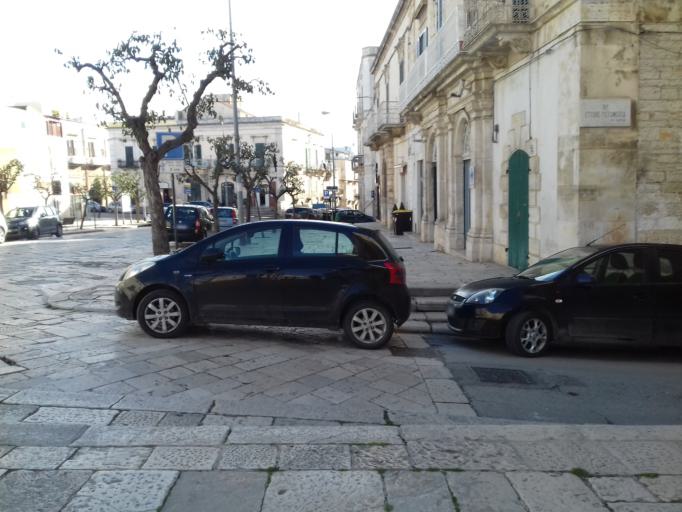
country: IT
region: Apulia
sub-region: Provincia di Bari
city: Ruvo di Puglia
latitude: 41.1168
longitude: 16.4833
